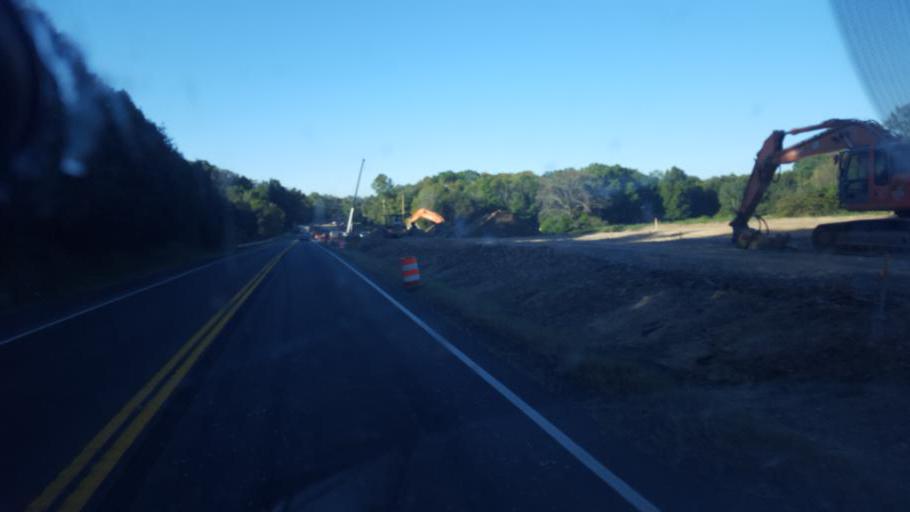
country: US
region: Virginia
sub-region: Prince William County
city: Nokesville
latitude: 38.7142
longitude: -77.5630
